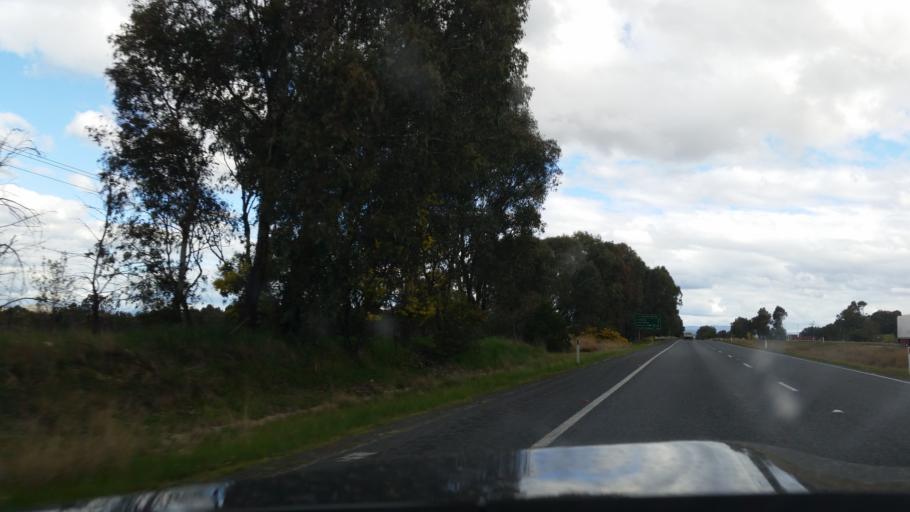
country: AU
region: New South Wales
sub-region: Albury Municipality
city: Lavington
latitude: -35.9805
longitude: 147.0005
